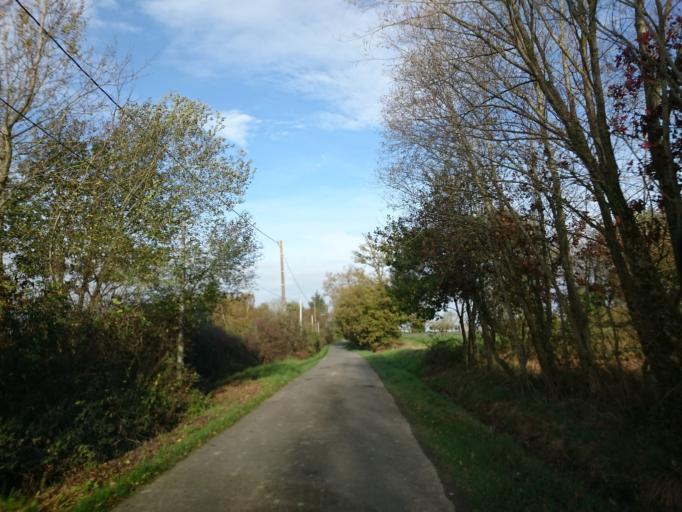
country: FR
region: Brittany
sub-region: Departement d'Ille-et-Vilaine
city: Chanteloup
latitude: 47.9582
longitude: -1.6458
